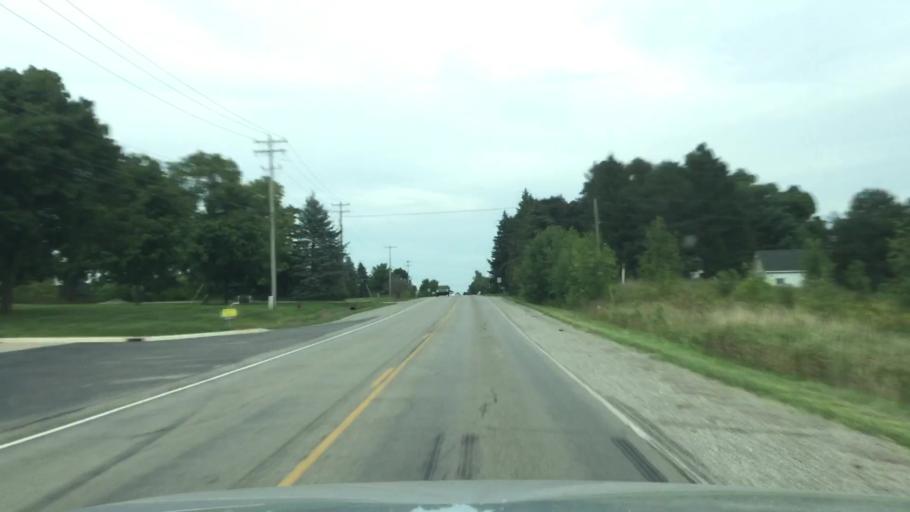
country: US
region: Michigan
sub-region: Genesee County
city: Grand Blanc
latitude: 42.8862
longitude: -83.6617
